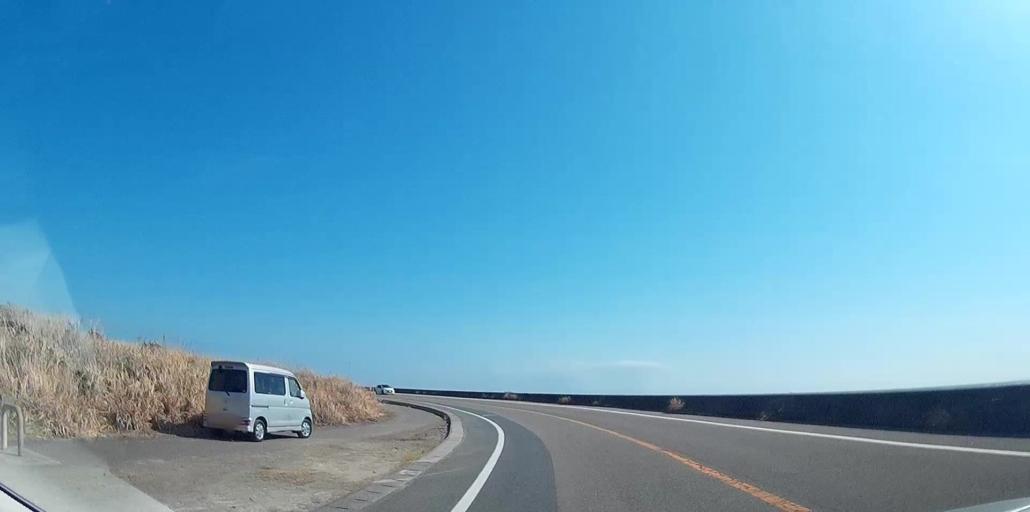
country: JP
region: Chiba
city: Tateyama
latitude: 34.9033
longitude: 139.8439
